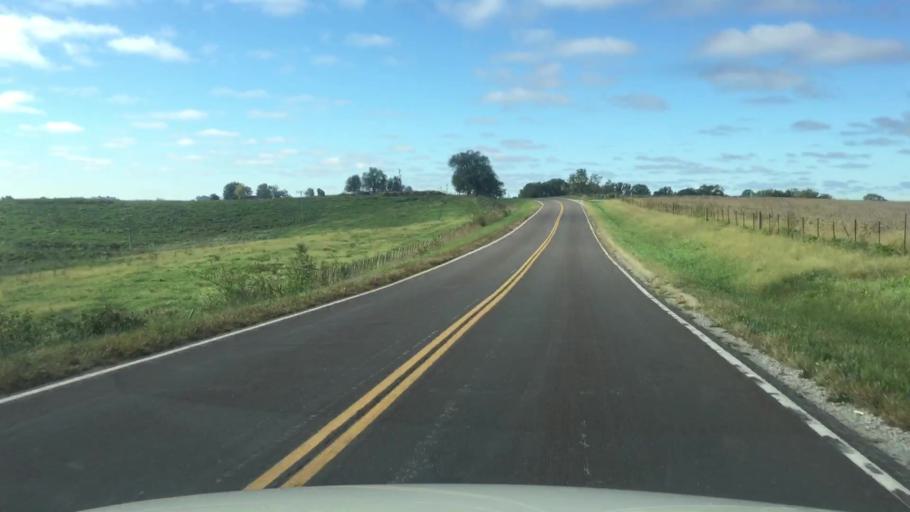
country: US
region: Missouri
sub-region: Howard County
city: Fayette
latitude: 39.0972
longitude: -92.7406
